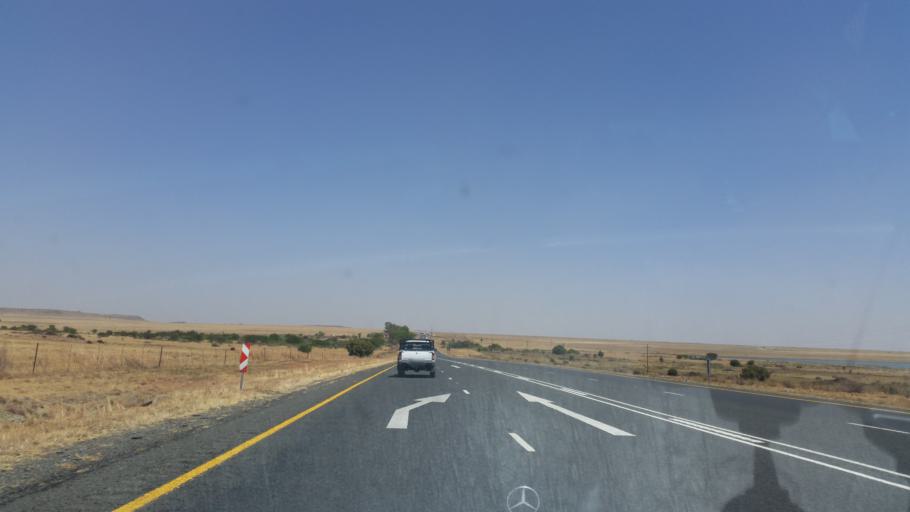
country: ZA
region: Orange Free State
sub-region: Lejweleputswa District Municipality
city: Brandfort
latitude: -28.7877
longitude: 26.7050
